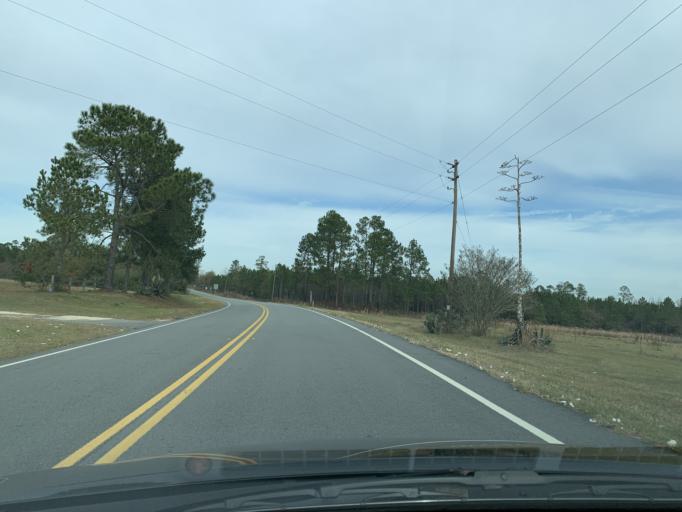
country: US
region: Georgia
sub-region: Wilcox County
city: Rochelle
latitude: 31.8441
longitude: -83.4248
